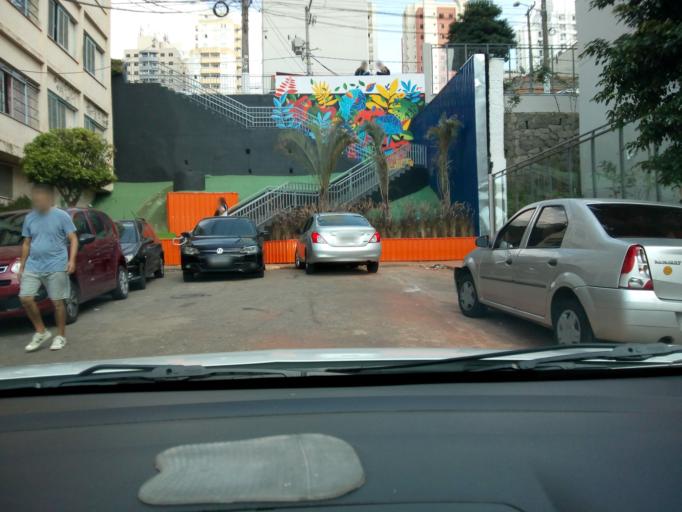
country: BR
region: Sao Paulo
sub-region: Sao Paulo
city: Sao Paulo
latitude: -23.5668
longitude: -46.6358
